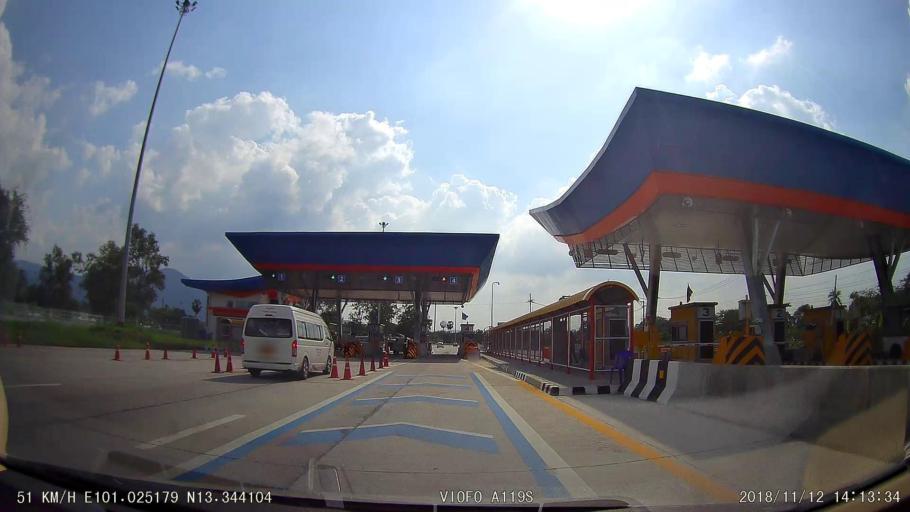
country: TH
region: Chon Buri
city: Chon Buri
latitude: 13.3440
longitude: 101.0251
